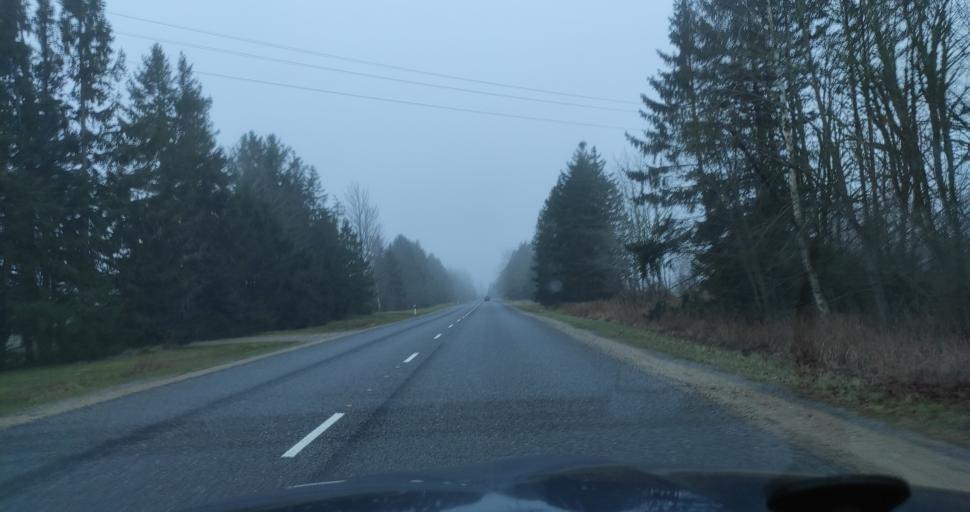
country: LV
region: Alsunga
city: Alsunga
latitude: 57.0048
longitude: 21.3861
